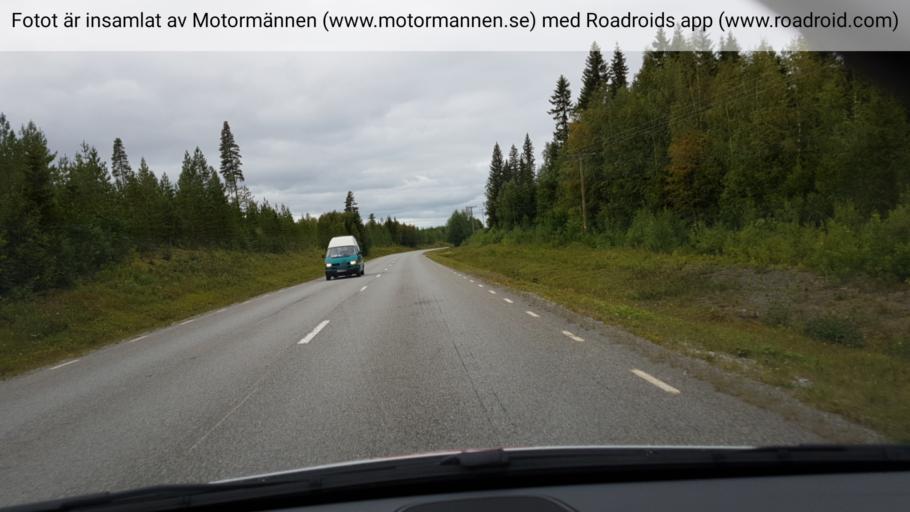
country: SE
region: Jaemtland
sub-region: Stroemsunds Kommun
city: Stroemsund
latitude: 64.2334
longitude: 15.4706
